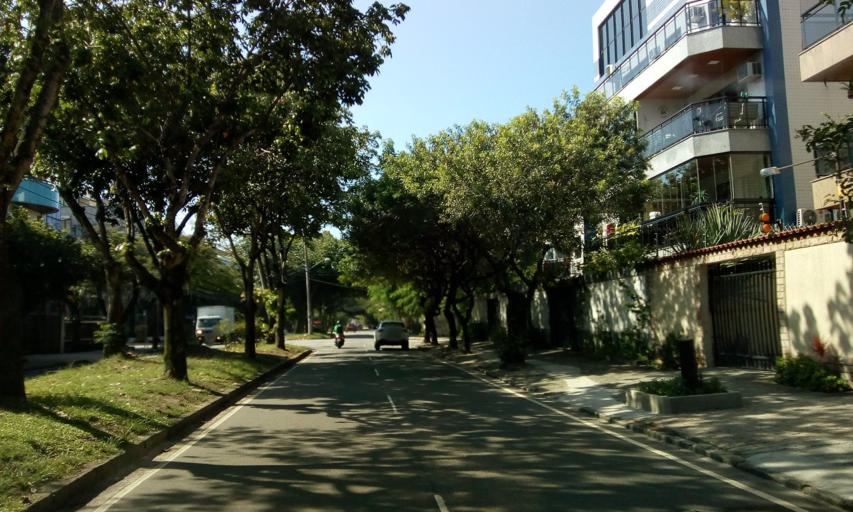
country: BR
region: Rio de Janeiro
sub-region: Nilopolis
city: Nilopolis
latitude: -23.0182
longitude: -43.4596
